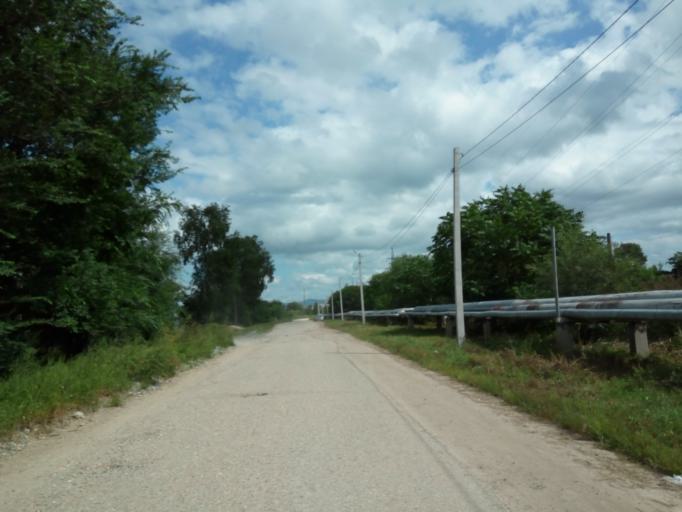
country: RU
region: Primorskiy
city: Dal'nerechensk
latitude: 45.9500
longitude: 133.8187
